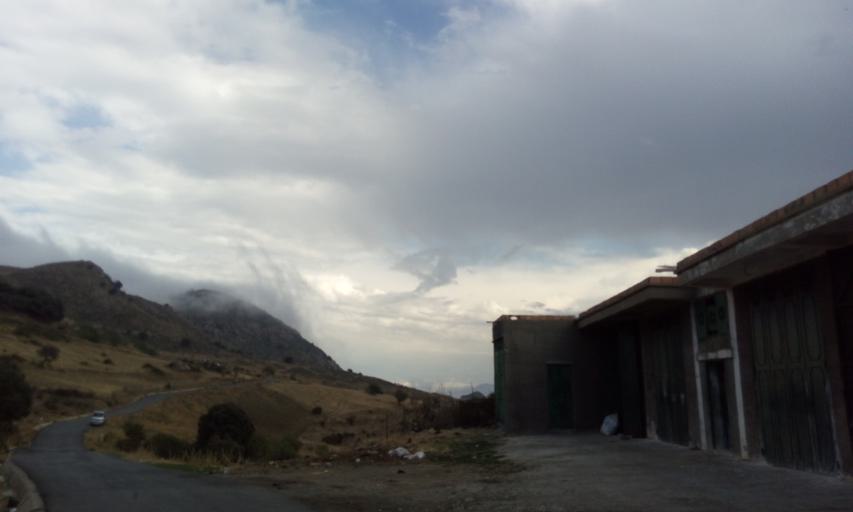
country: DZ
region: Tizi Ouzou
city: Chemini
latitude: 36.6039
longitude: 4.5717
